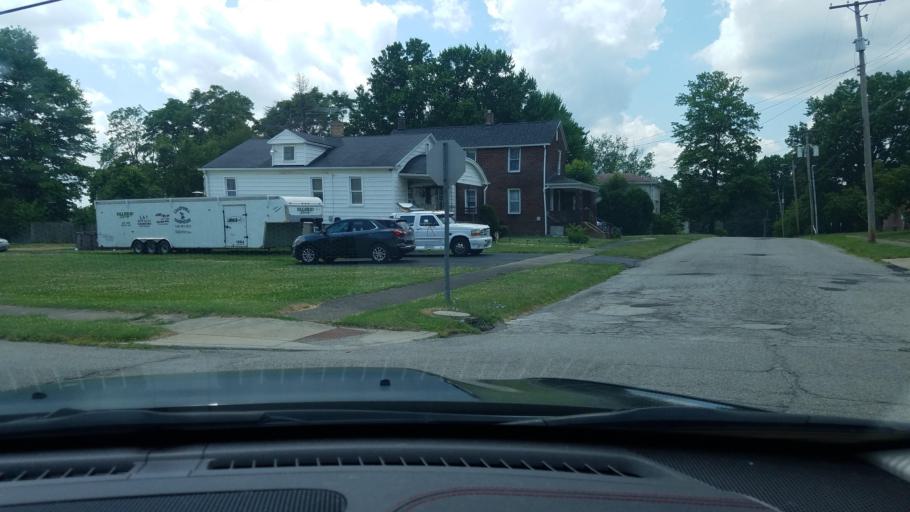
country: US
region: Ohio
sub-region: Mahoning County
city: Campbell
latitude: 41.0765
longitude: -80.5937
